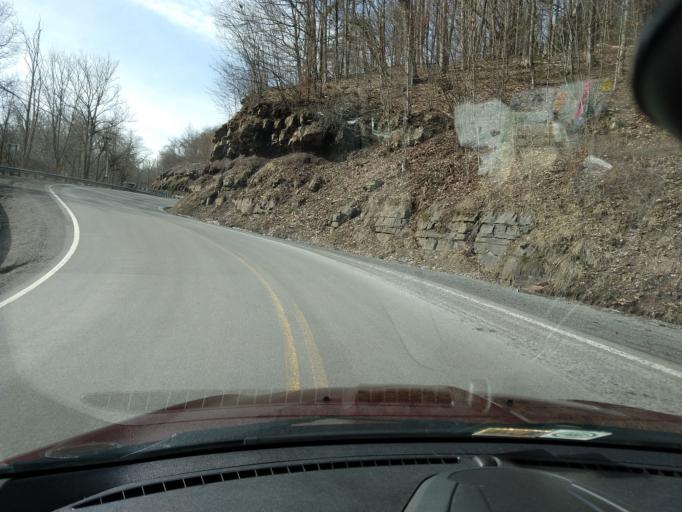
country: US
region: West Virginia
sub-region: Pocahontas County
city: Marlinton
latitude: 38.1134
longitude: -80.2626
